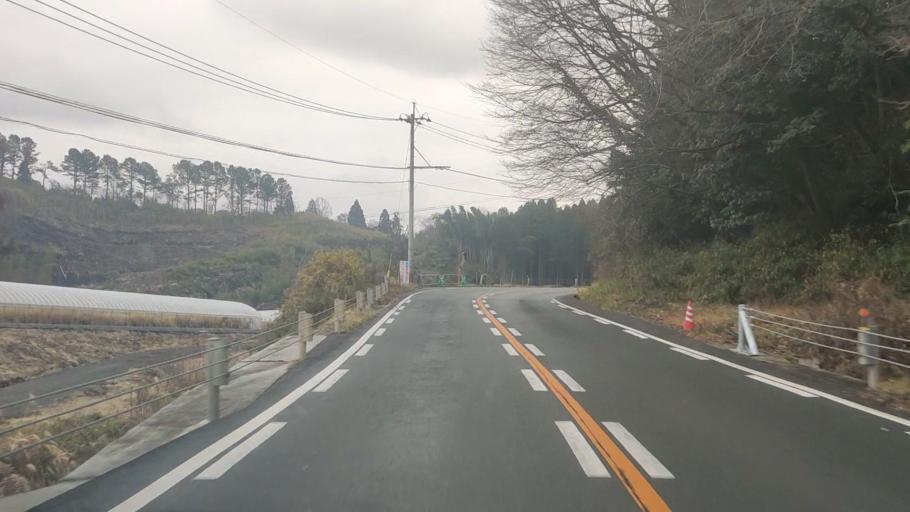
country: JP
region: Kumamoto
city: Aso
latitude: 32.8998
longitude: 130.9993
